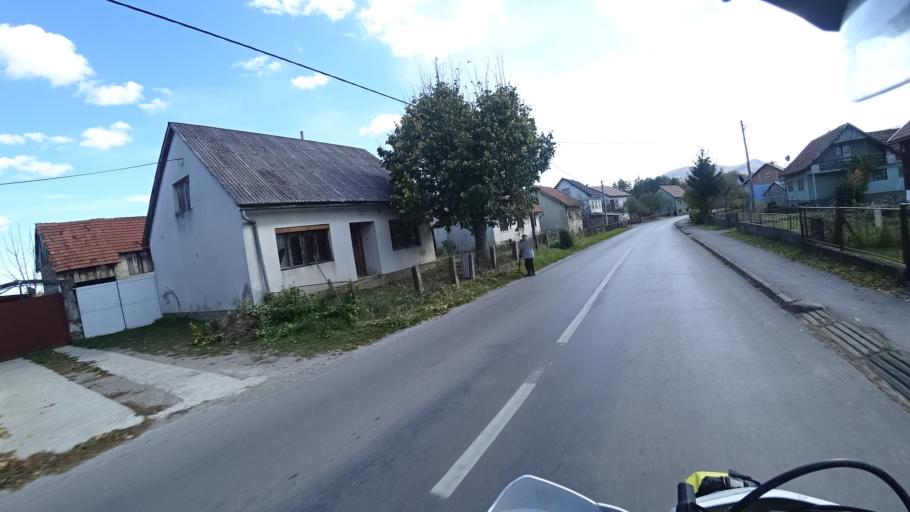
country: HR
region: Karlovacka
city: Plaski
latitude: 45.0873
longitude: 15.3661
